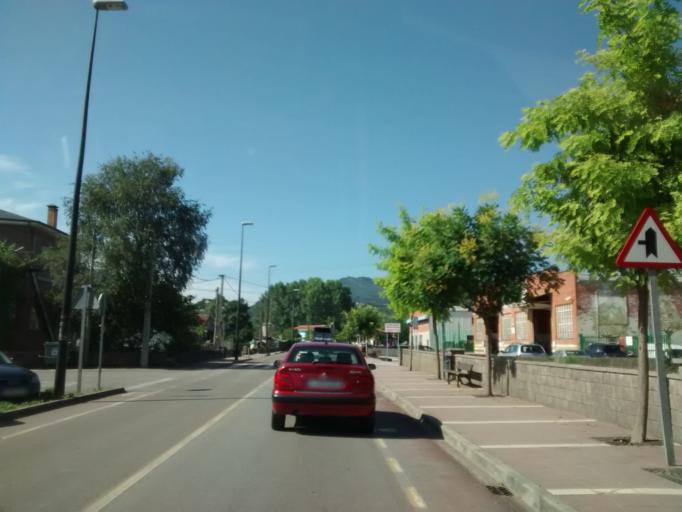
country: ES
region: Cantabria
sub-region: Provincia de Cantabria
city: Cartes
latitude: 43.3316
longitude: -4.0661
